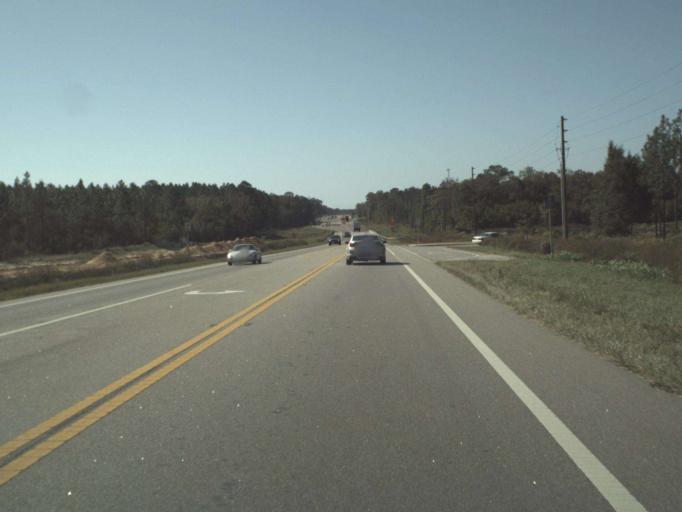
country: US
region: Florida
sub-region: Walton County
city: Freeport
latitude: 30.4991
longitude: -86.1183
